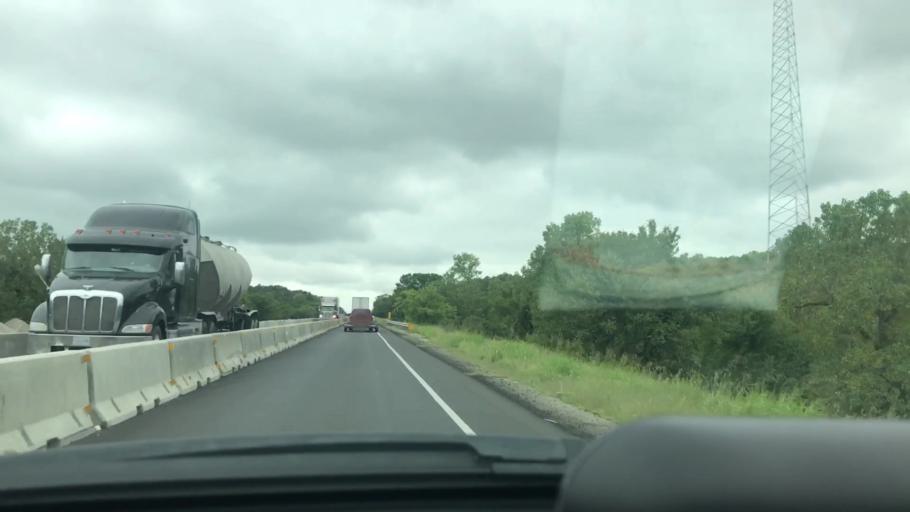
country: US
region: Oklahoma
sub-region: McIntosh County
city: Eufaula
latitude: 35.2646
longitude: -95.5899
